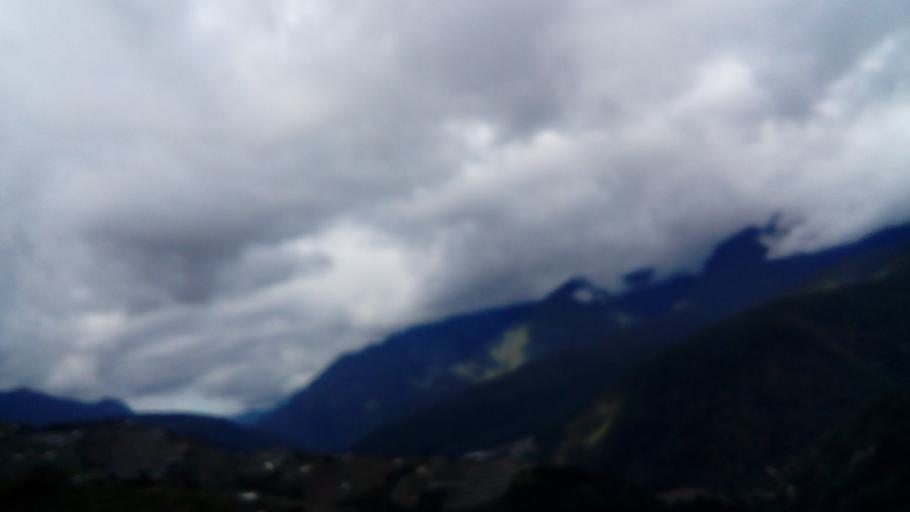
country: TW
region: Taiwan
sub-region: Nantou
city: Puli
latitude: 24.2611
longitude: 121.2587
